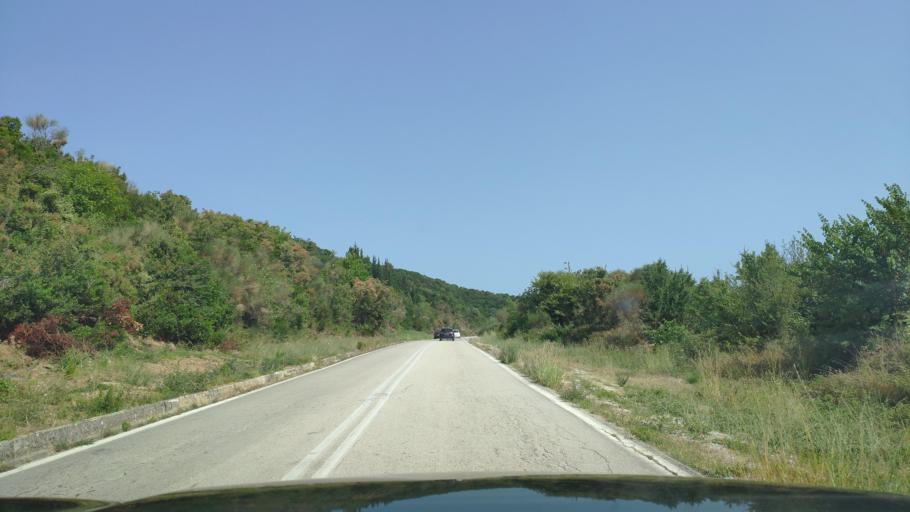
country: GR
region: Epirus
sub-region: Nomos Artas
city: Peta
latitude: 39.1702
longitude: 21.0687
